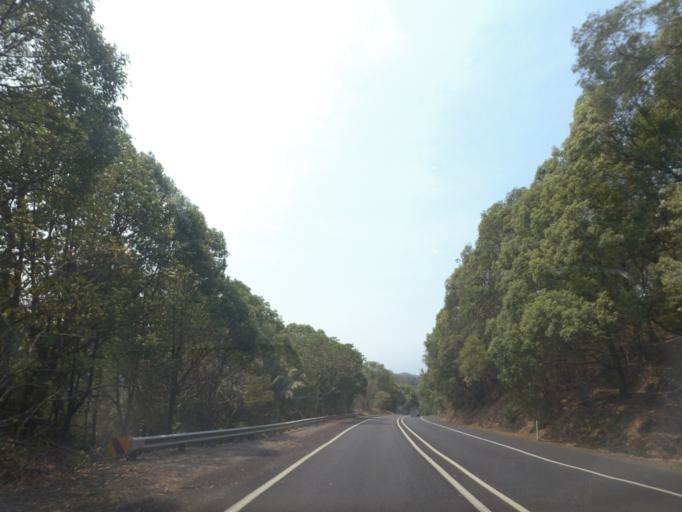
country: AU
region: New South Wales
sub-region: Byron Shire
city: Brunswick Heads
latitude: -28.5184
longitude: 153.5283
